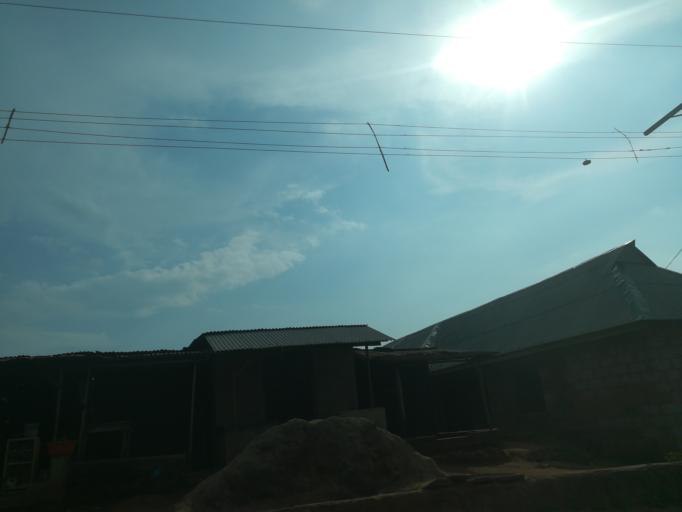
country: NG
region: Lagos
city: Ikorodu
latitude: 6.6631
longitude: 3.6697
